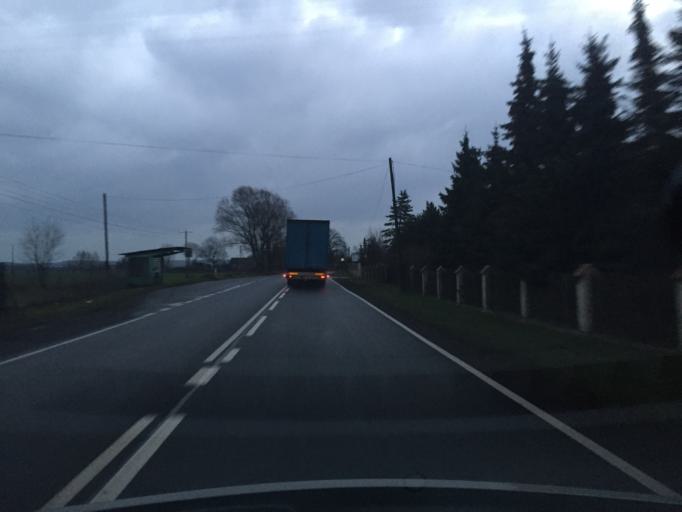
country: PL
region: Kujawsko-Pomorskie
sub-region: Powiat brodnicki
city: Bobrowo
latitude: 53.2350
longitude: 19.2778
